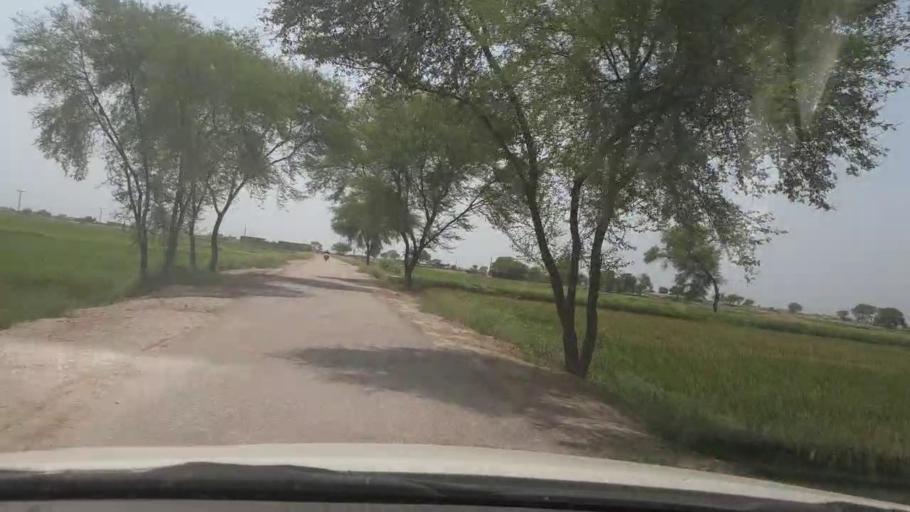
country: PK
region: Sindh
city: Shikarpur
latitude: 27.9936
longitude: 68.5772
